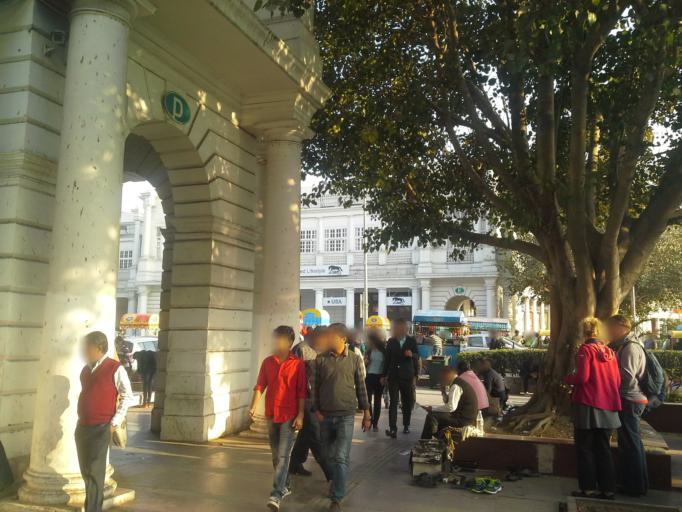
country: IN
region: NCT
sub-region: New Delhi
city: New Delhi
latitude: 28.6337
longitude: 77.2210
